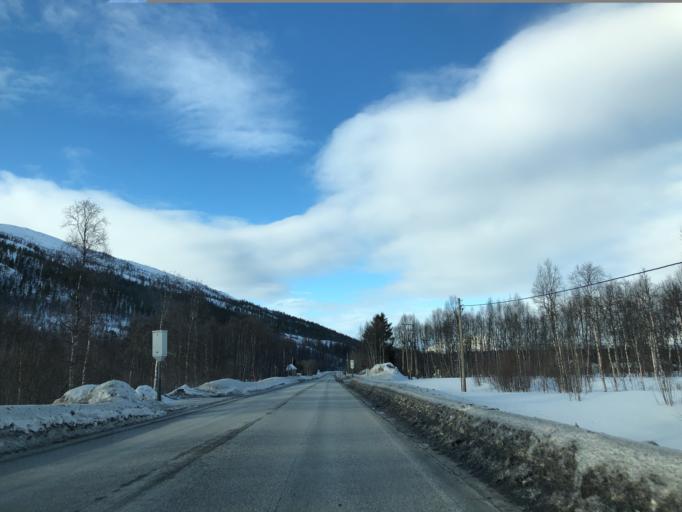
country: NO
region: Troms
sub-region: Malselv
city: Moen
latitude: 69.1177
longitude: 18.5838
